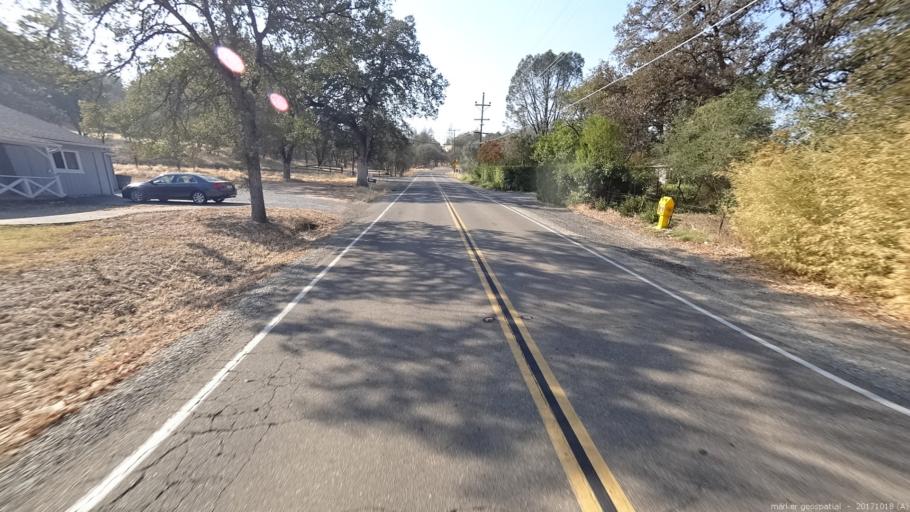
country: US
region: California
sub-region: Shasta County
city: Palo Cedro
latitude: 40.5637
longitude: -122.2452
